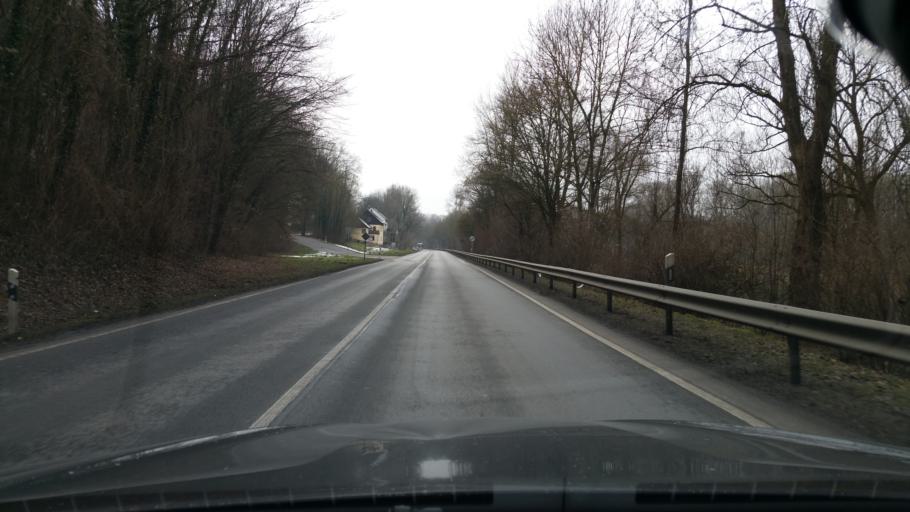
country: DE
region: Bavaria
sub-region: Lower Bavaria
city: Landshut
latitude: 48.5266
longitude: 12.1331
